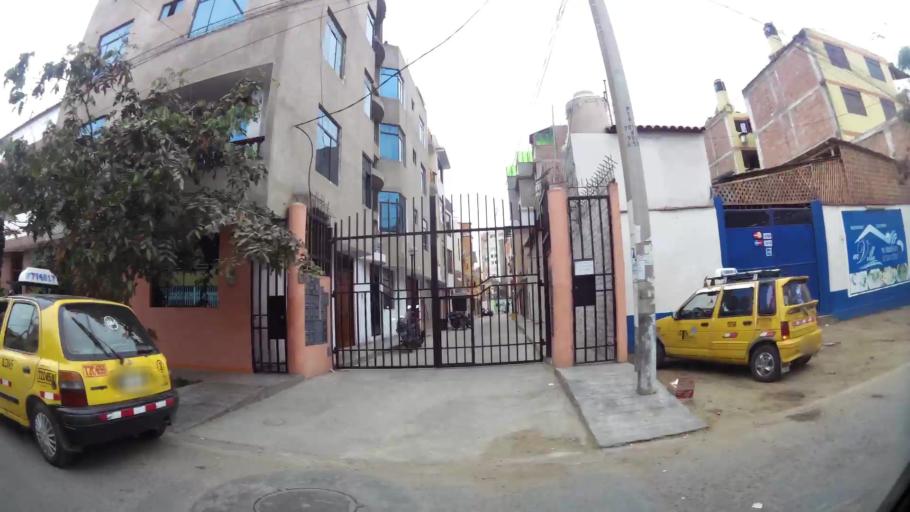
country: PE
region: La Libertad
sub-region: Provincia de Trujillo
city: La Esperanza
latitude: -8.0954
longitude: -79.0427
